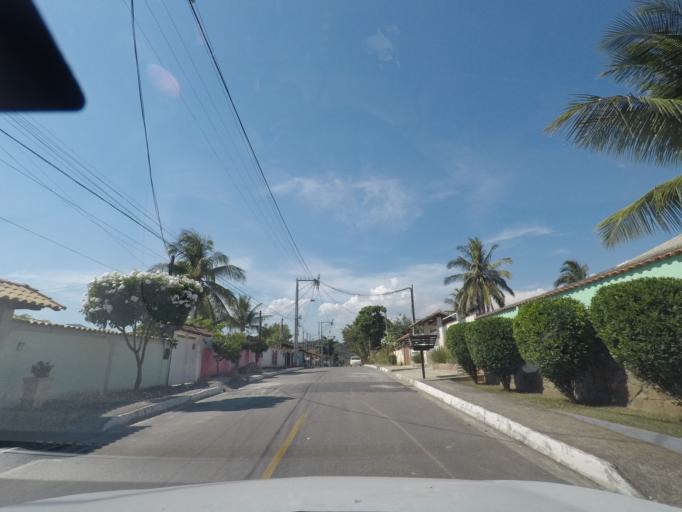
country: BR
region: Rio de Janeiro
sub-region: Niteroi
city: Niteroi
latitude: -22.9658
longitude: -42.9702
